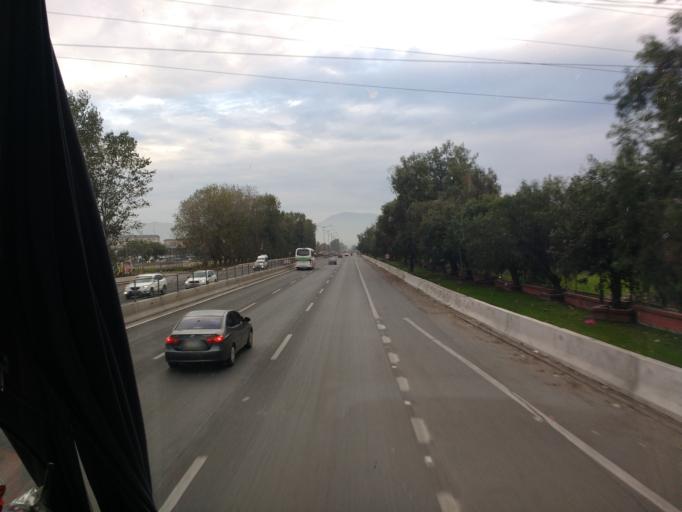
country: CL
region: Santiago Metropolitan
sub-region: Provincia de Santiago
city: Lo Prado
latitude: -33.4549
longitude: -70.7309
